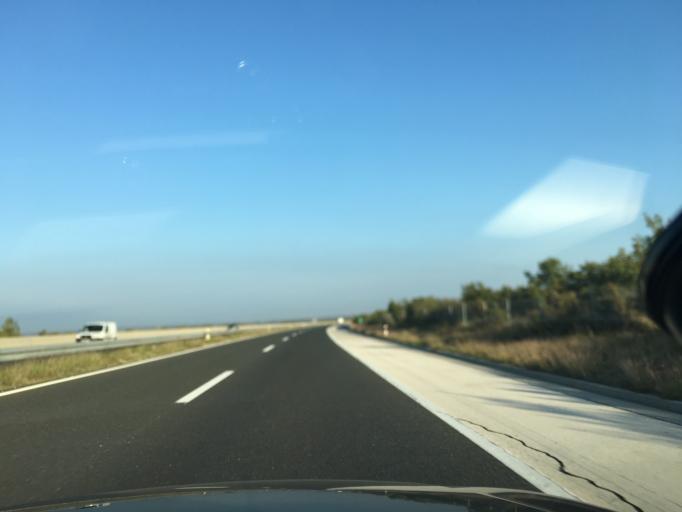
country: HR
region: Zadarska
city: Galovac
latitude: 44.1252
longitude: 15.4285
